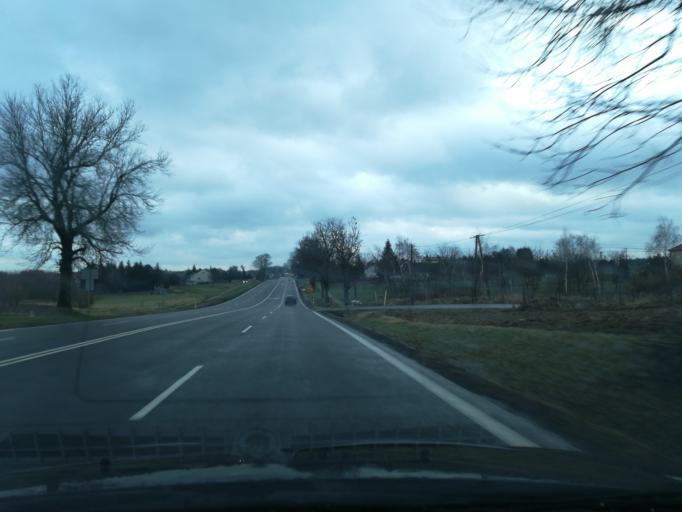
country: PL
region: Subcarpathian Voivodeship
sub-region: Powiat lancucki
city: Kosina
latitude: 50.0738
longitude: 22.3149
